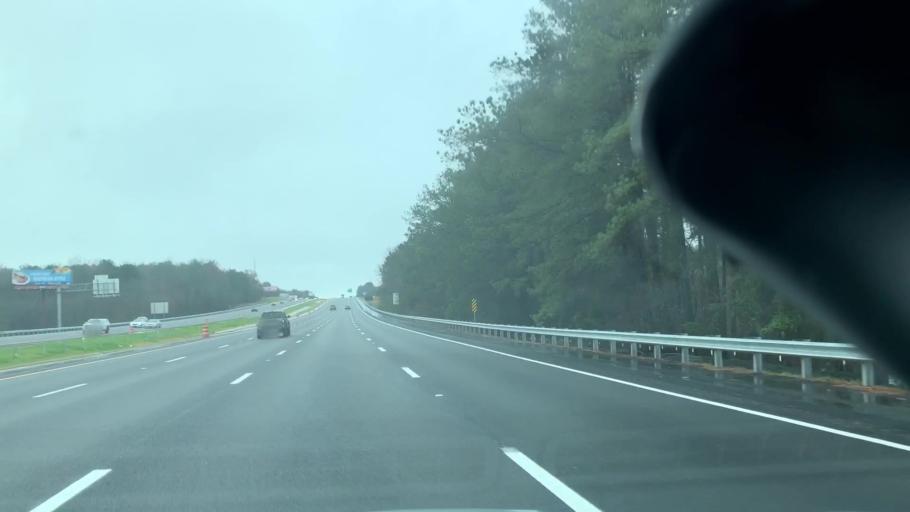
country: US
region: South Carolina
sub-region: Richland County
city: Dentsville
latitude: 34.1254
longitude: -80.9626
